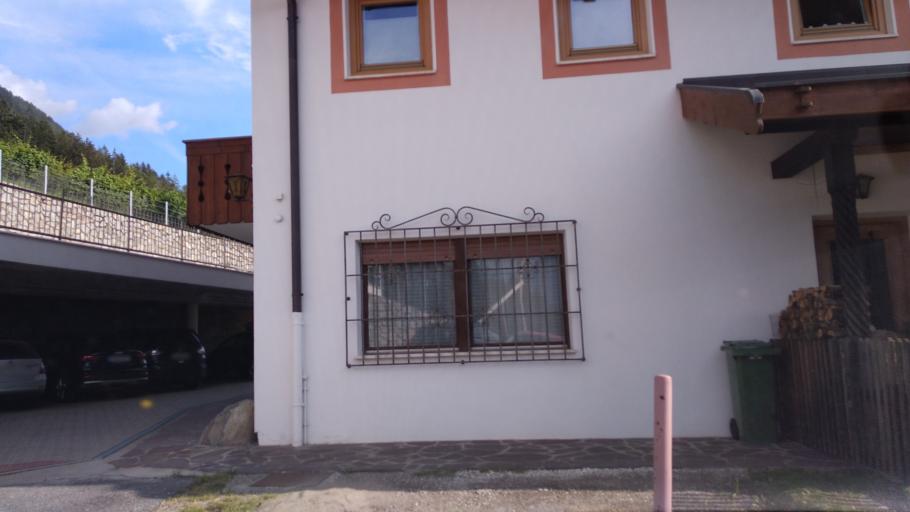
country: IT
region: Trentino-Alto Adige
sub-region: Bolzano
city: Scena
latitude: 46.6926
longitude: 11.2000
